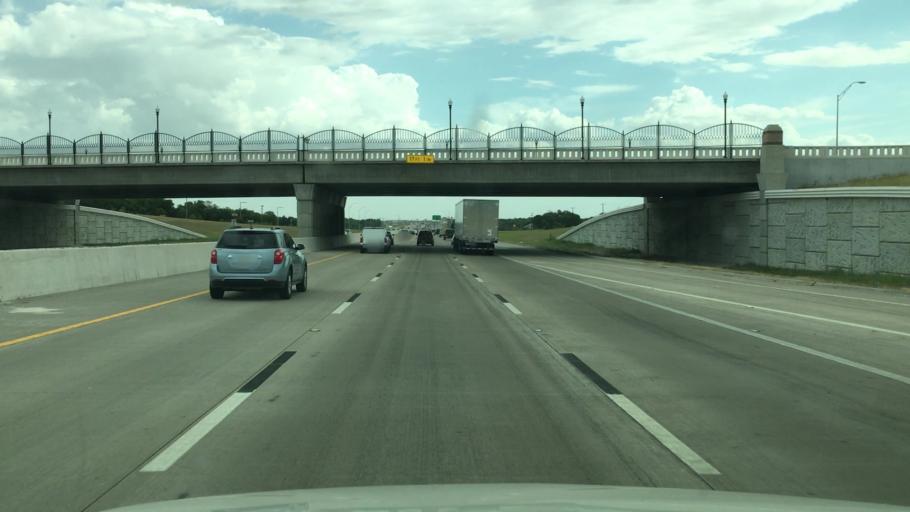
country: US
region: Texas
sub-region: McLennan County
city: Lorena
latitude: 31.3811
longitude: -97.2137
